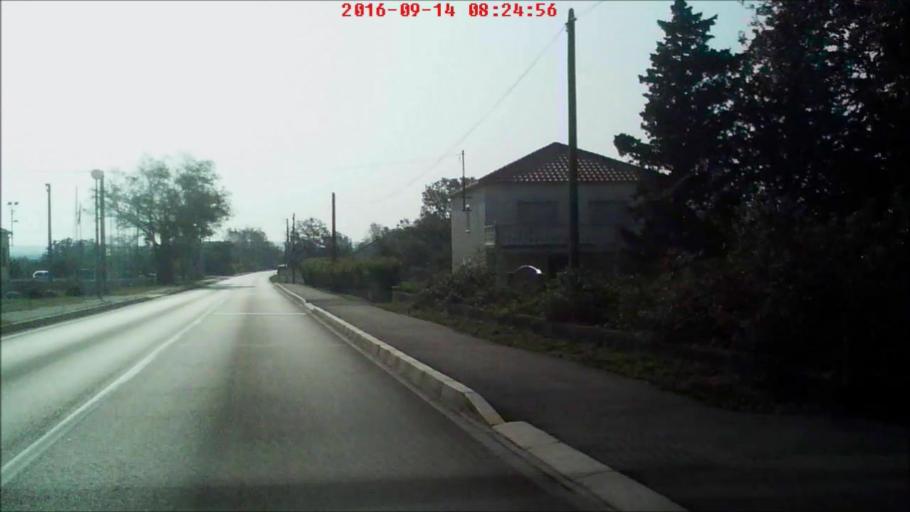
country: HR
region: Zadarska
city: Vrsi
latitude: 44.2054
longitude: 15.2502
